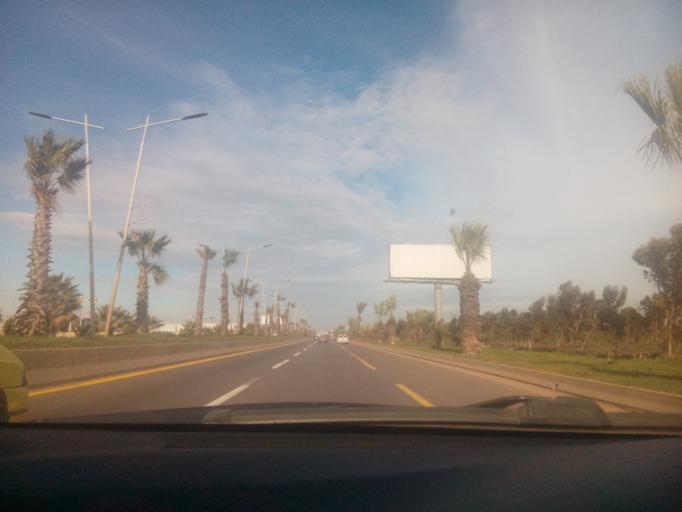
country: DZ
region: Oran
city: Es Senia
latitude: 35.6310
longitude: -0.5870
